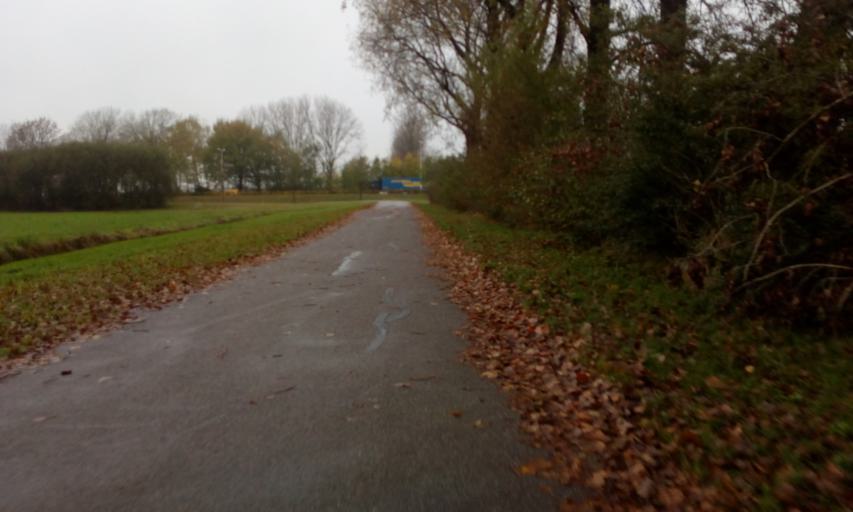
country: NL
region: South Holland
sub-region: Gemeente Lansingerland
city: Berkel en Rodenrijs
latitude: 51.9723
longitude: 4.4851
